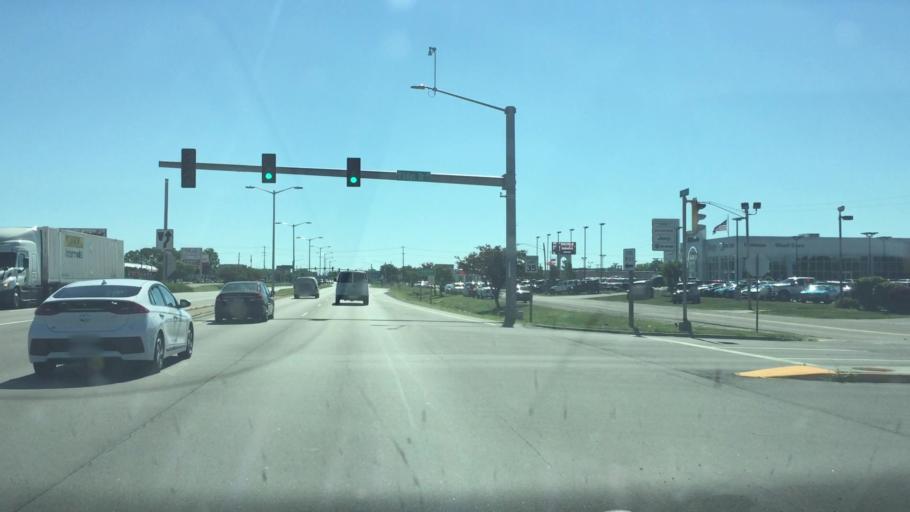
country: US
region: Wisconsin
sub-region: Outagamie County
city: Appleton
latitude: 44.2618
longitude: -88.4510
